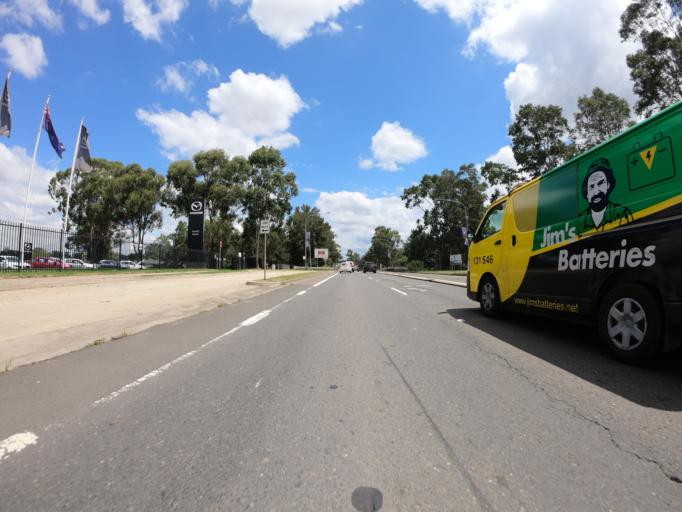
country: AU
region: New South Wales
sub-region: Penrith Municipality
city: Glenmore Park
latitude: -33.7673
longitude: 150.6786
